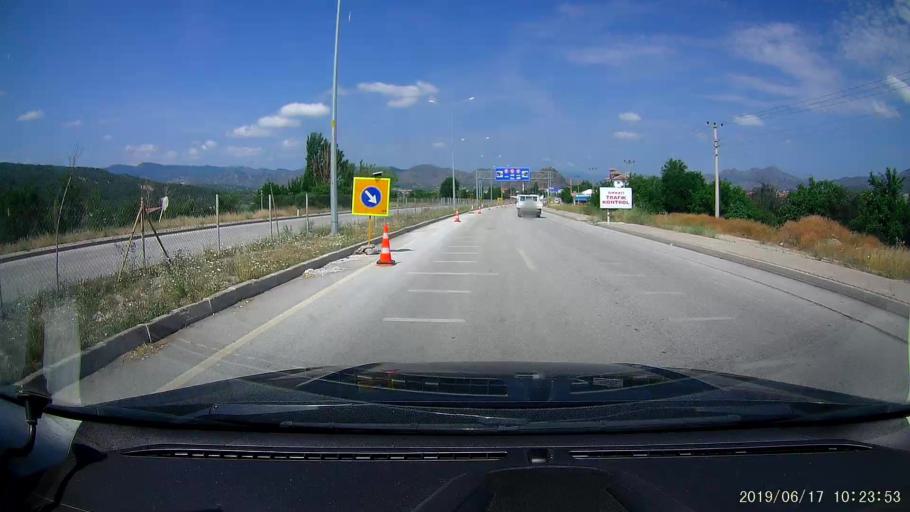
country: TR
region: Corum
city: Osmancik
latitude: 40.9704
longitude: 34.8306
